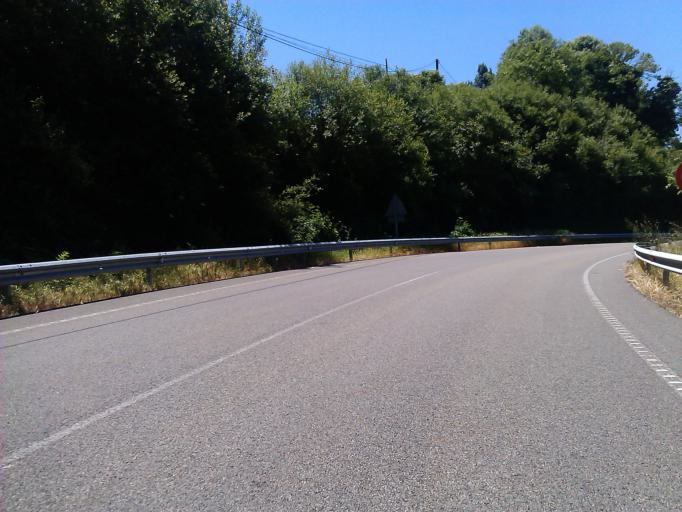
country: ES
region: Galicia
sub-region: Provincia de Lugo
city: Samos
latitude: 42.7400
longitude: -7.2874
